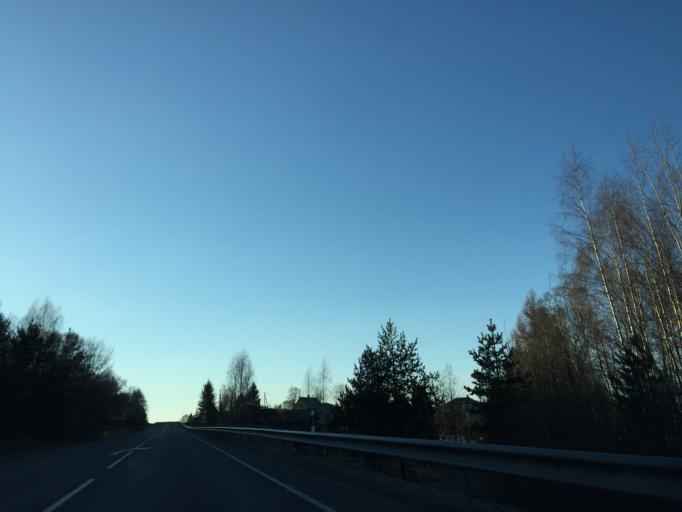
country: EE
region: Ida-Virumaa
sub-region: Johvi vald
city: Johvi
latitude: 59.2006
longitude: 27.5403
